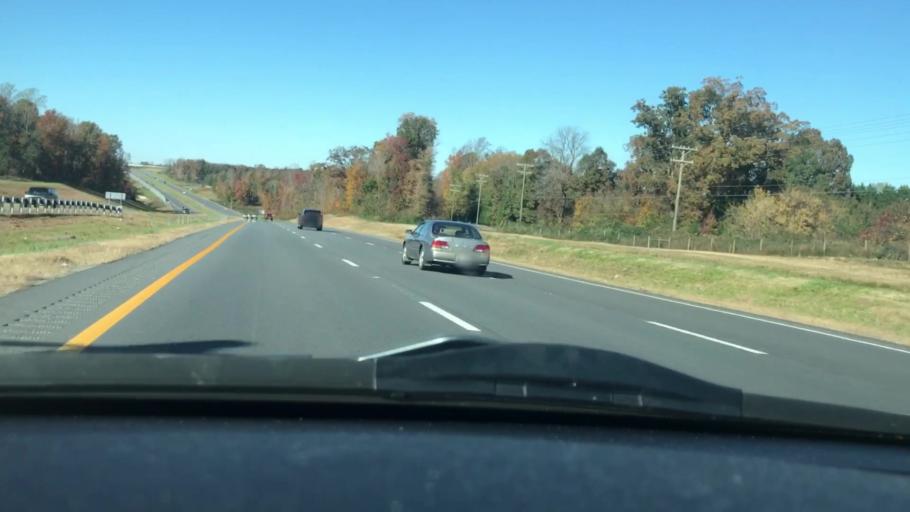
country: US
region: North Carolina
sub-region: Guilford County
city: Summerfield
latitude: 36.2509
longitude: -79.9220
